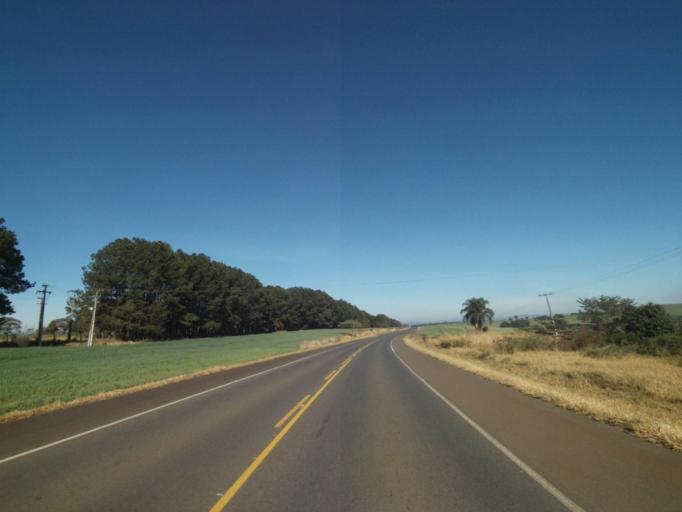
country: BR
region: Parana
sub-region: Tibagi
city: Tibagi
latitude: -24.4151
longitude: -50.3663
